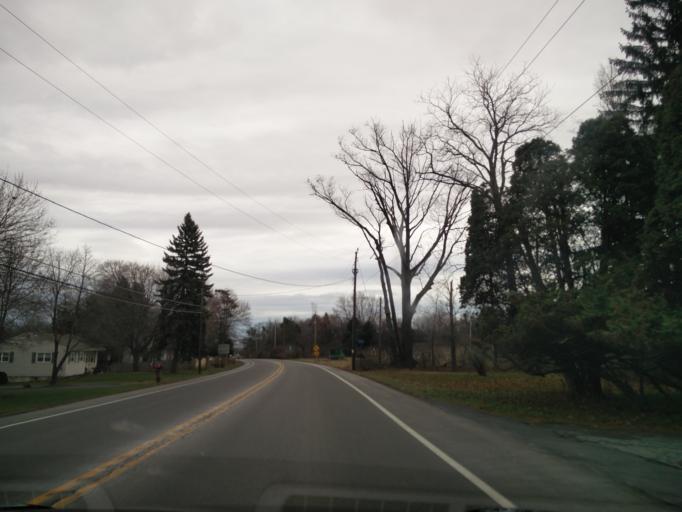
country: US
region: New York
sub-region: Tompkins County
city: Northwest Ithaca
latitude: 42.4739
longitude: -76.5526
